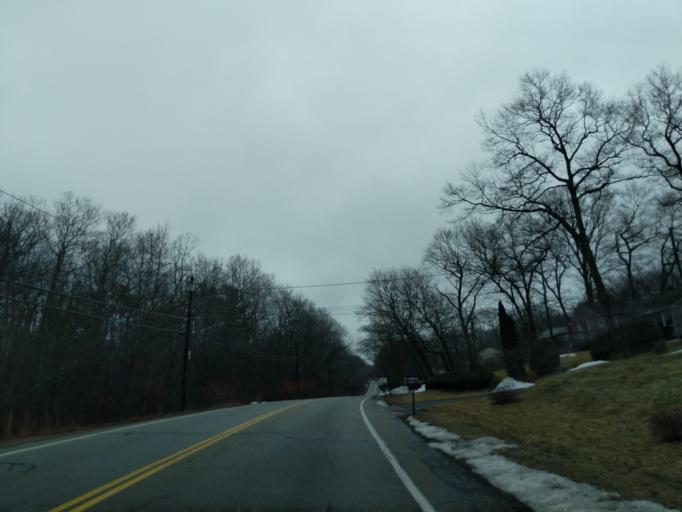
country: US
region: Massachusetts
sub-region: Worcester County
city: Webster
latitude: 42.0583
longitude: -71.8272
